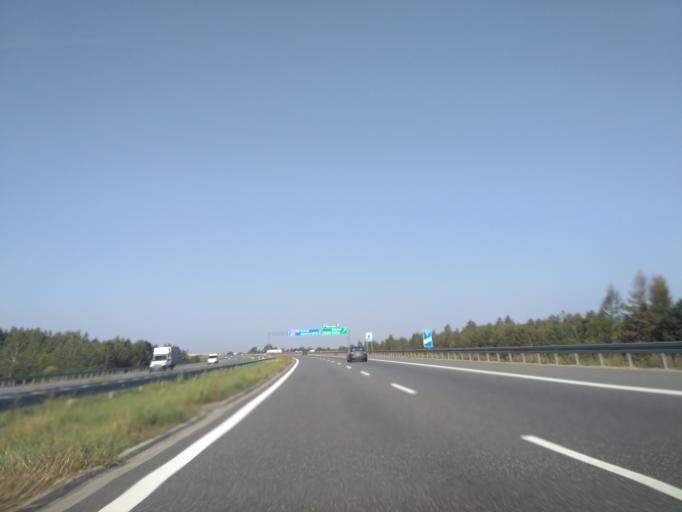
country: PL
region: Subcarpathian Voivodeship
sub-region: Powiat rzeszowski
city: Rudna Mala
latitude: 50.1075
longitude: 21.9876
